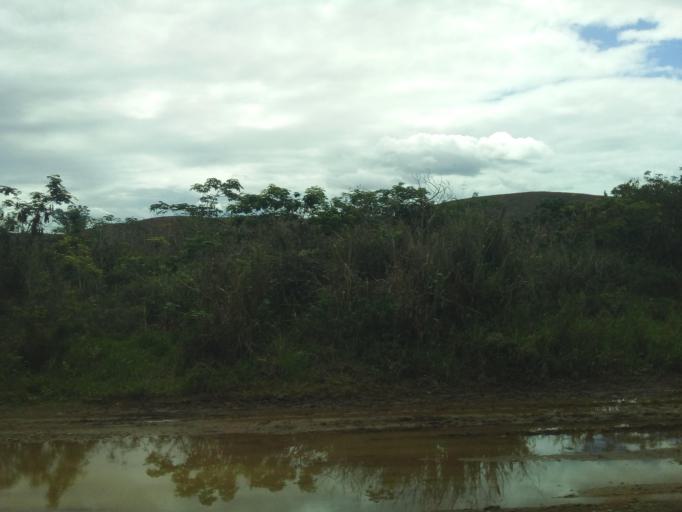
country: BR
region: Minas Gerais
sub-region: Governador Valadares
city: Governador Valadares
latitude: -19.0872
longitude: -42.1627
